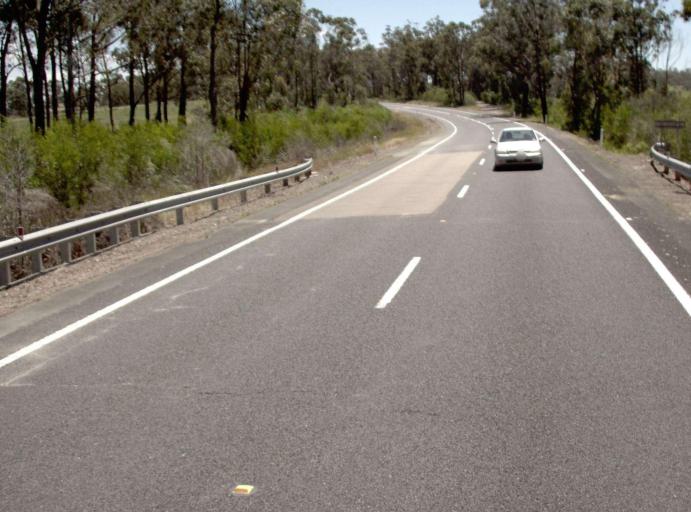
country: AU
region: Victoria
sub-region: East Gippsland
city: Lakes Entrance
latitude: -37.7538
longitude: 148.2966
